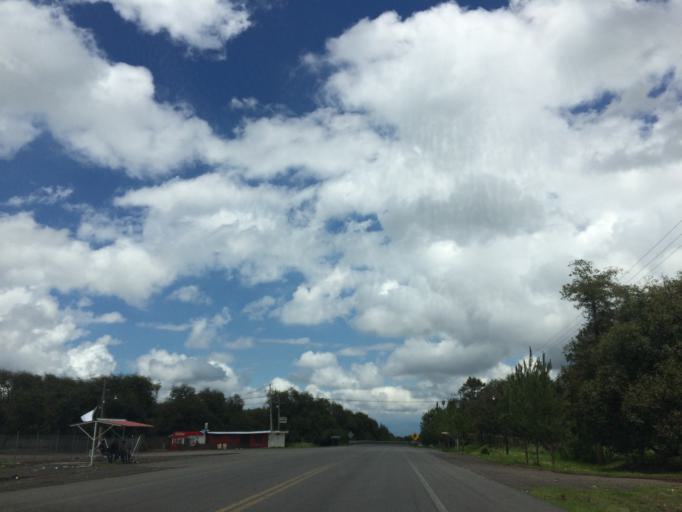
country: MX
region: Michoacan
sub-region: Uruapan
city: Santa Ana Zirosto
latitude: 19.5429
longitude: -102.3284
